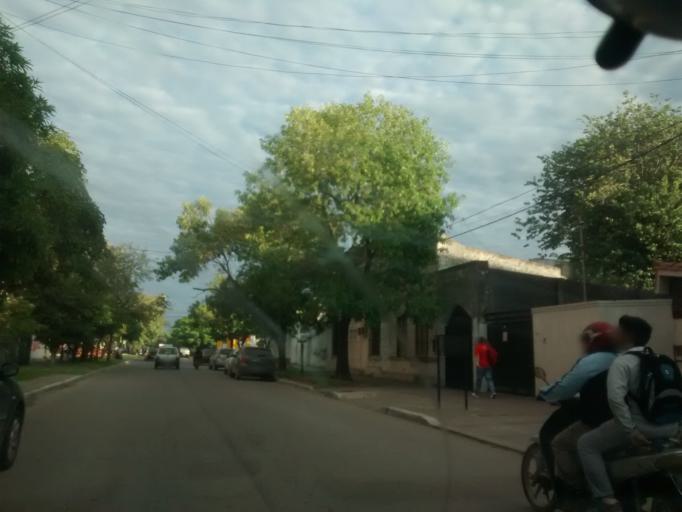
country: AR
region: Chaco
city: Resistencia
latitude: -27.4612
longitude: -58.9822
